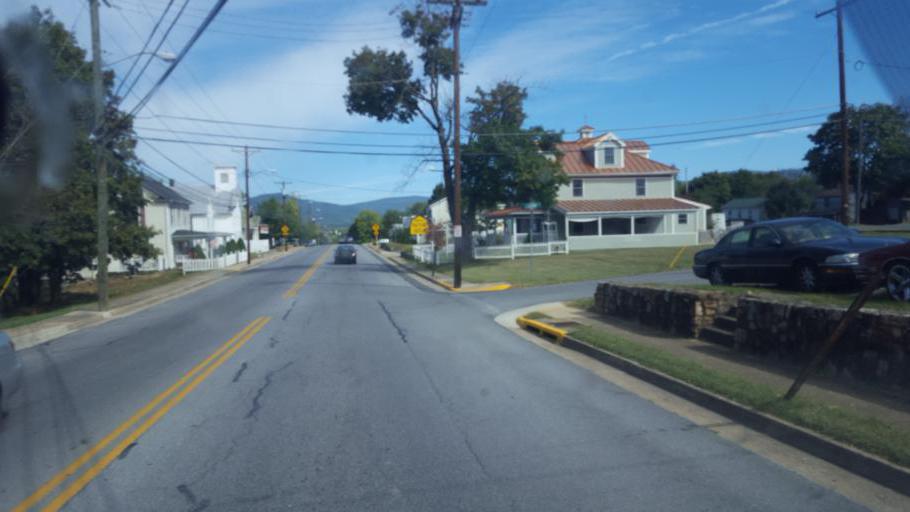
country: US
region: Virginia
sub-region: Page County
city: Luray
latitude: 38.6644
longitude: -78.4740
